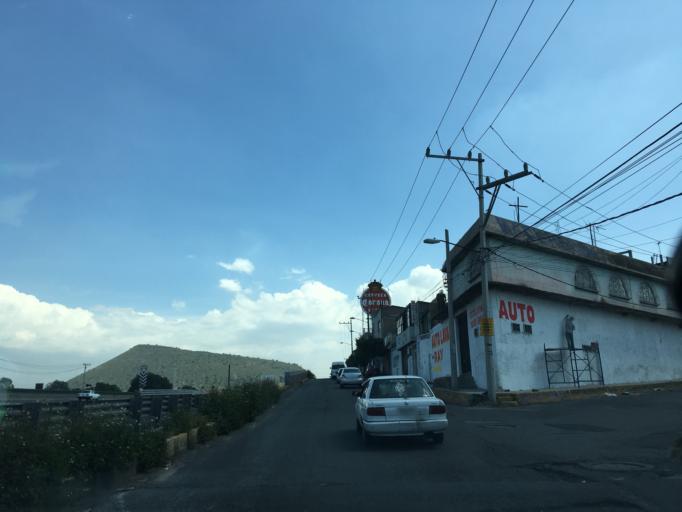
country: MX
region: Mexico
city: Los Reyes La Paz
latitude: 19.3544
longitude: -98.9908
